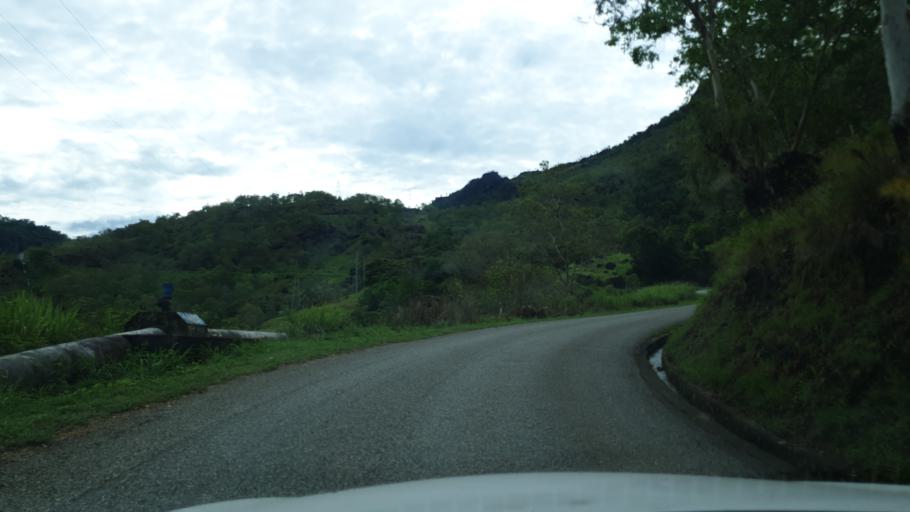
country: PG
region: National Capital
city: Port Moresby
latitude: -9.4194
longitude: 147.3595
